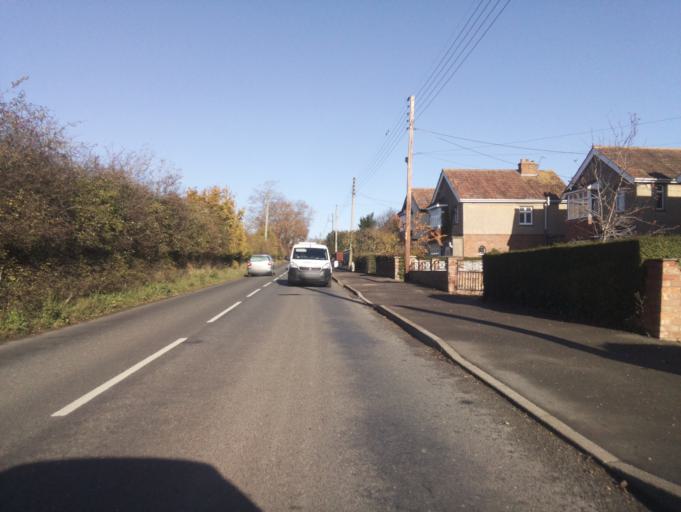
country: GB
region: England
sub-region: Somerset
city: Langport
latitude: 51.0438
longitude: -2.8244
